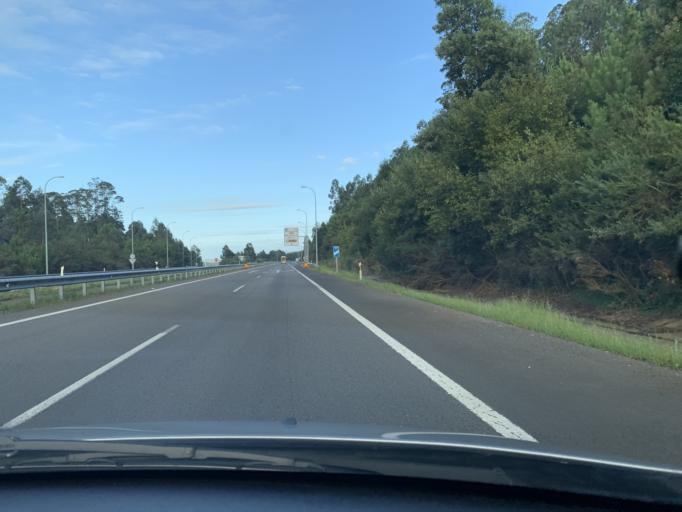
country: ES
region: Galicia
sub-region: Provincia de Lugo
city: Barreiros
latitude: 43.5380
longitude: -7.1584
